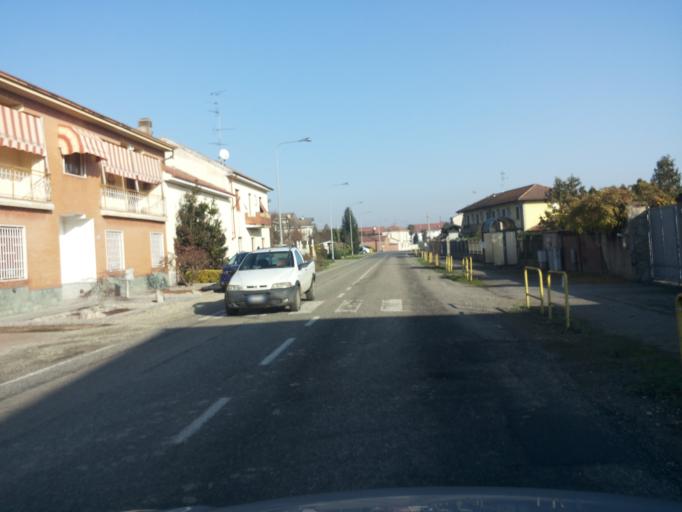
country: IT
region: Piedmont
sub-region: Provincia di Vercelli
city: Desana
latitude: 45.2646
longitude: 8.3535
